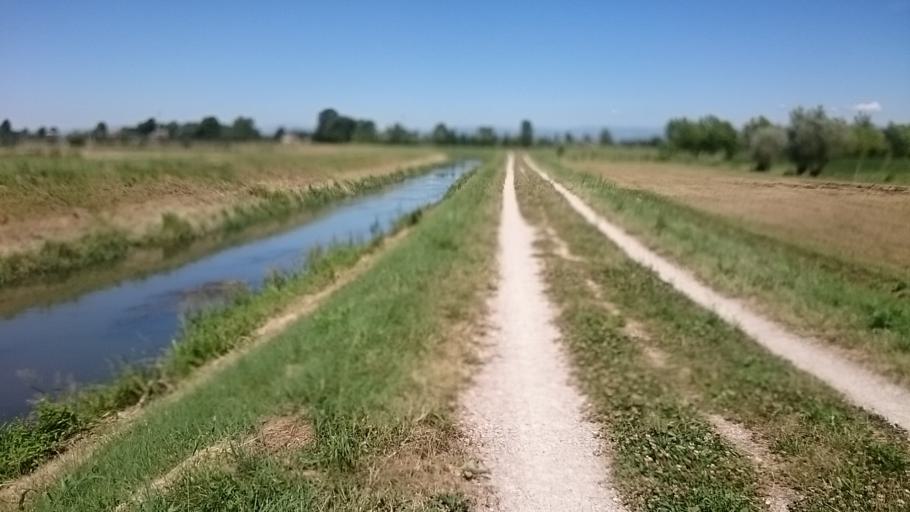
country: IT
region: Veneto
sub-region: Provincia di Padova
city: Pionca
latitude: 45.4670
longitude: 11.9587
